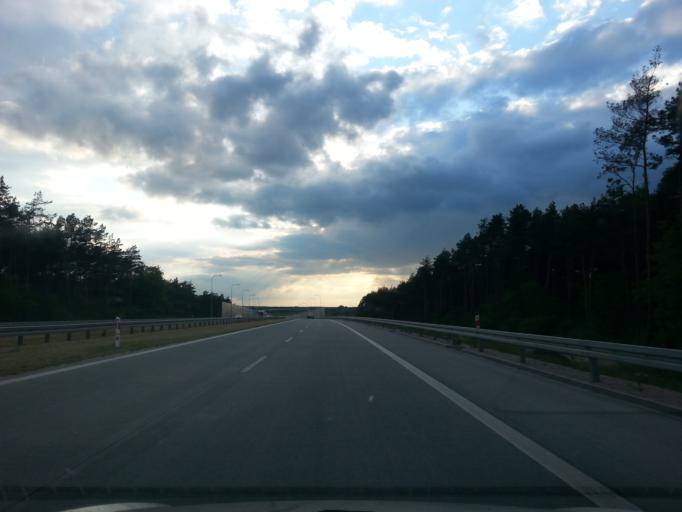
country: PL
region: Lodz Voivodeship
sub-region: Powiat zdunskowolski
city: Zdunska Wola
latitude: 51.5738
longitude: 18.9511
